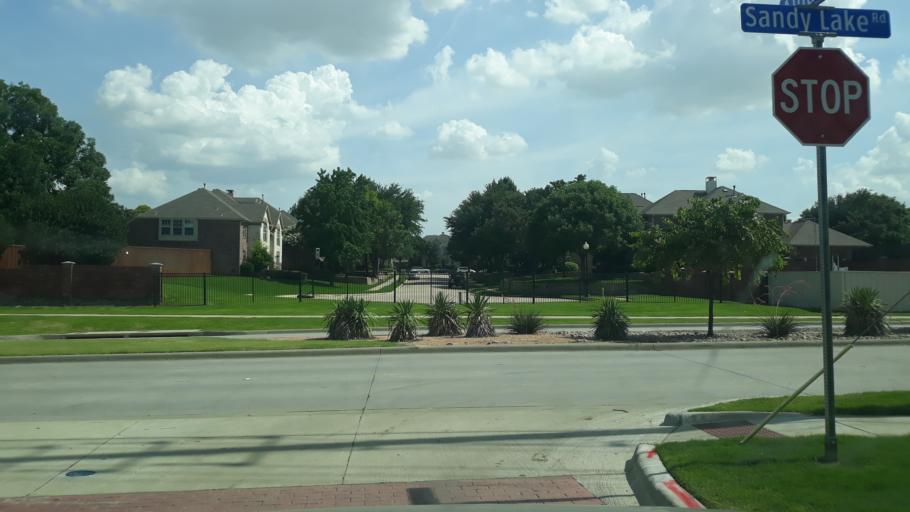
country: US
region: Texas
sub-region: Dallas County
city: Coppell
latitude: 32.9699
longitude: -97.0024
